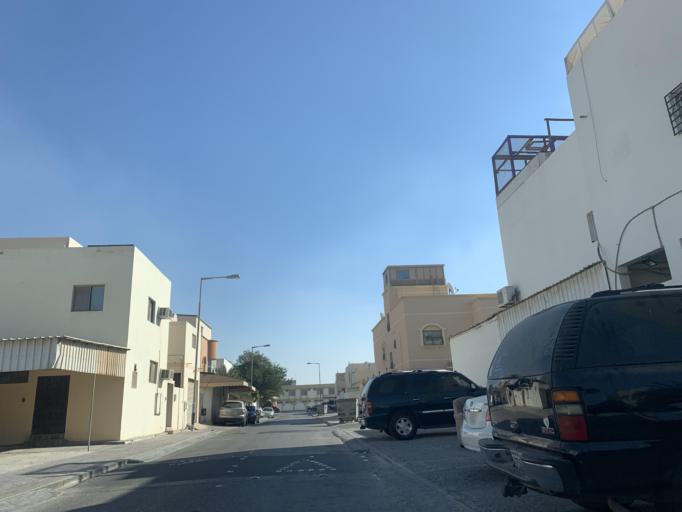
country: BH
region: Central Governorate
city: Madinat Hamad
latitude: 26.1161
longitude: 50.5075
